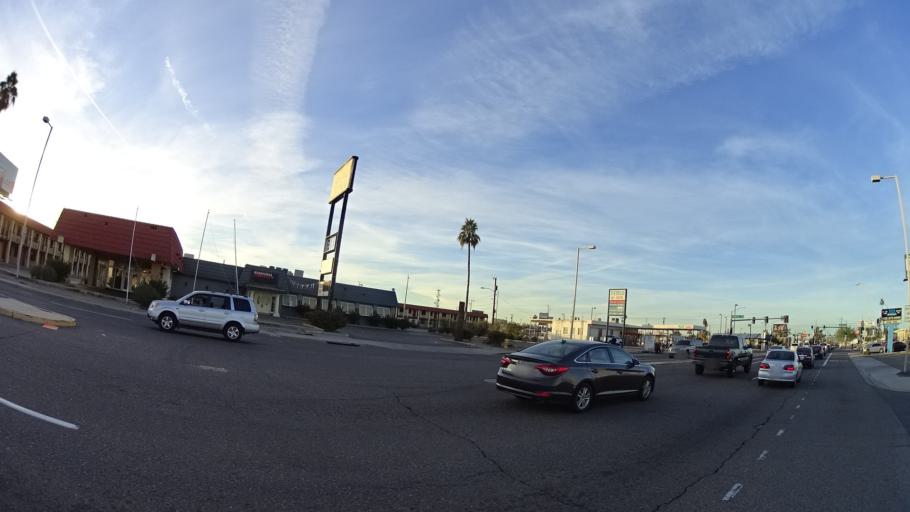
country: US
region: Arizona
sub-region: Maricopa County
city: Phoenix
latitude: 33.4463
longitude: -112.0300
